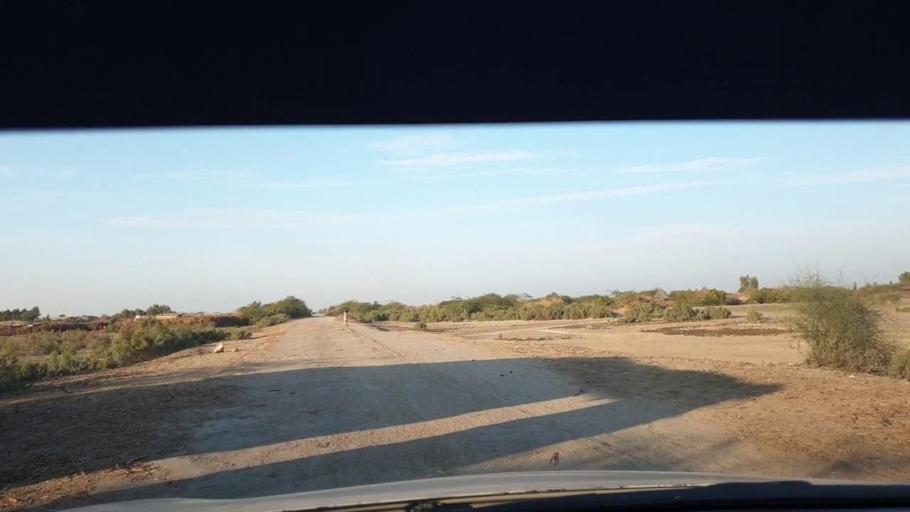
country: PK
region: Sindh
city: Berani
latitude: 25.8021
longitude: 68.8825
